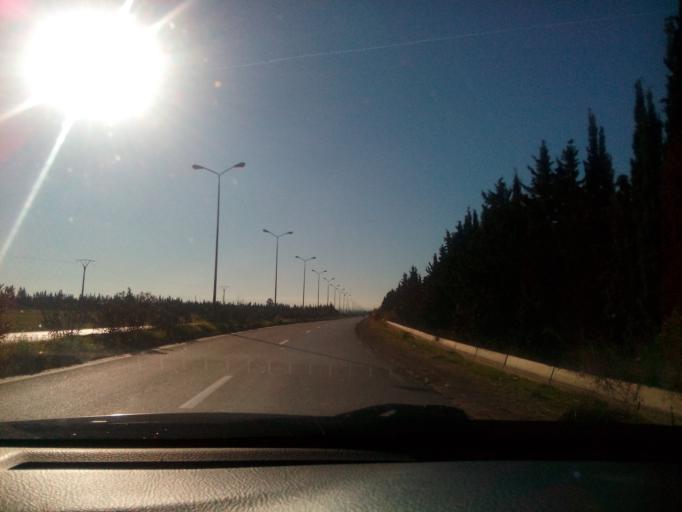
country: DZ
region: Relizane
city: Relizane
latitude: 35.7254
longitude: 0.5864
